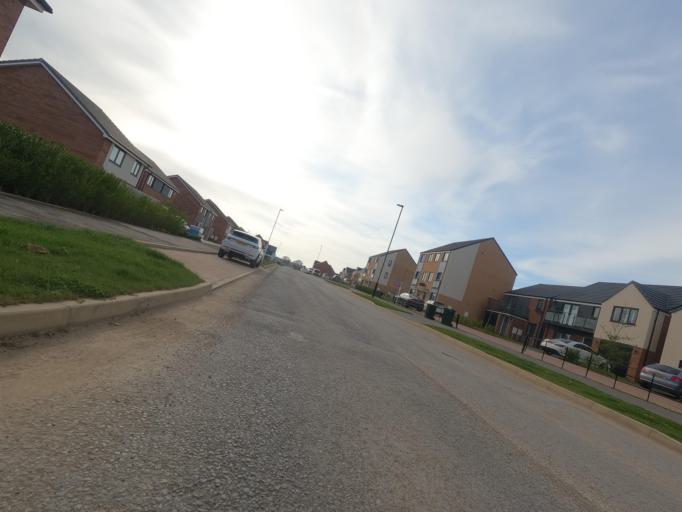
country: GB
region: England
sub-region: Newcastle upon Tyne
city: Hazlerigg
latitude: 55.0279
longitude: -1.6575
